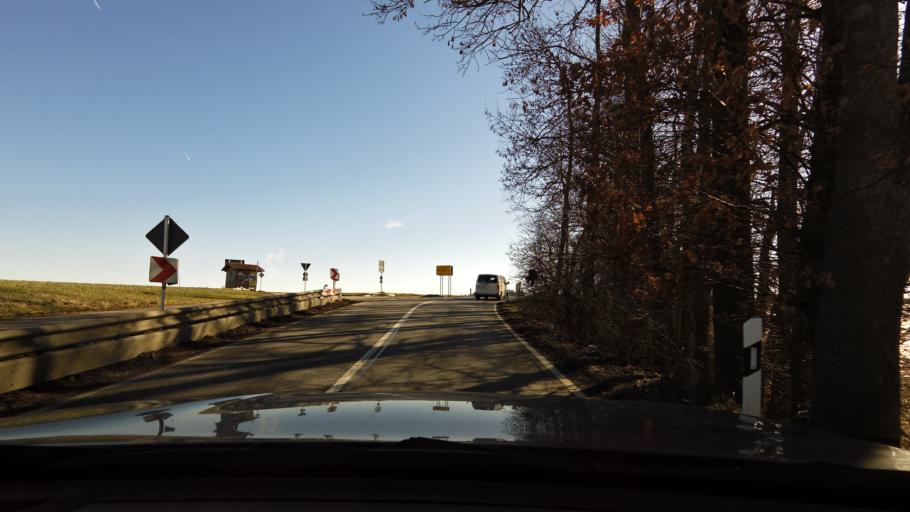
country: DE
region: Bavaria
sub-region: Upper Bavaria
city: Taufkirchen
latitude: 48.1371
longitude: 12.4553
